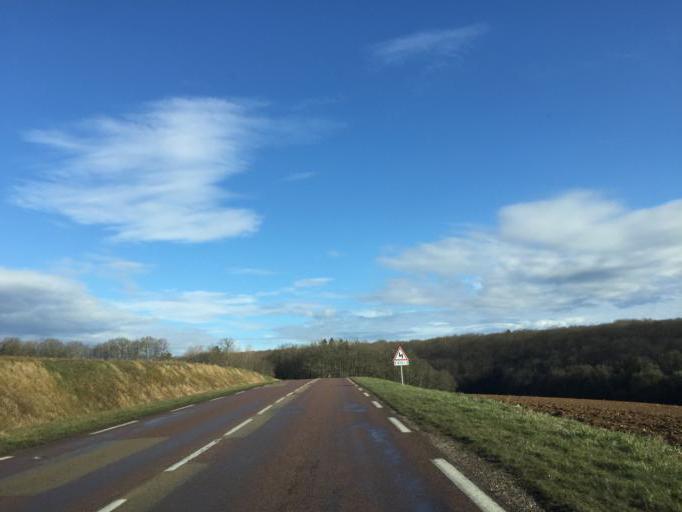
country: FR
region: Bourgogne
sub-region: Departement de la Nievre
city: Clamecy
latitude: 47.4553
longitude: 3.6767
